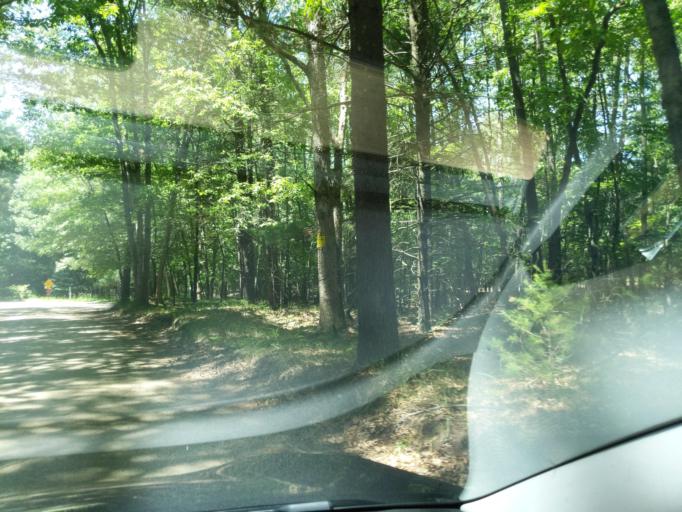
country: US
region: Michigan
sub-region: Muskegon County
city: Montague
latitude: 43.3875
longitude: -86.4208
